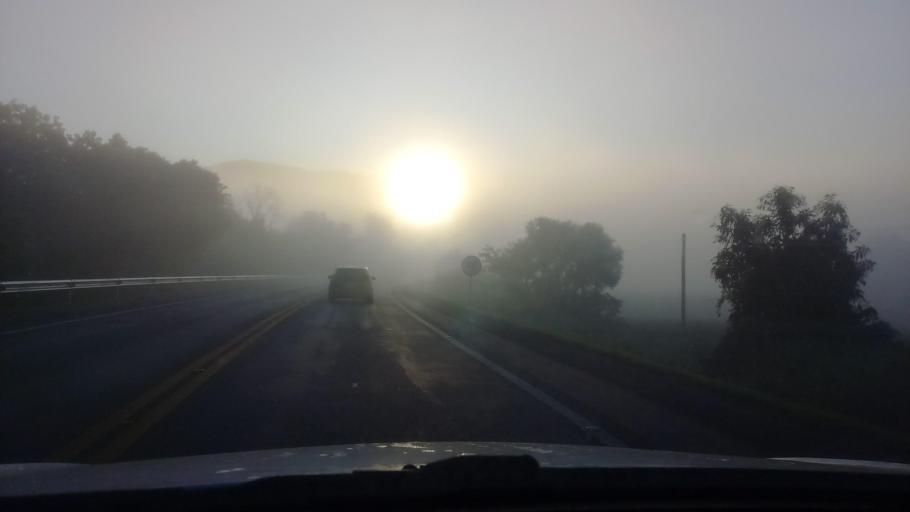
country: BR
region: Rio Grande do Sul
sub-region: Candelaria
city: Candelaria
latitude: -29.6685
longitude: -52.7664
